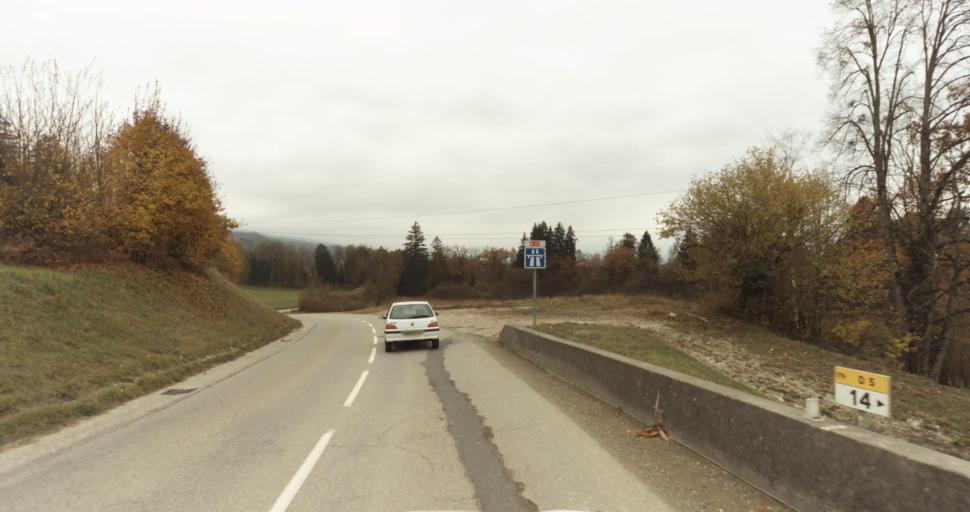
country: FR
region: Rhone-Alpes
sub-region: Departement de la Haute-Savoie
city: Viuz-la-Chiesaz
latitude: 45.8497
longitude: 6.0670
